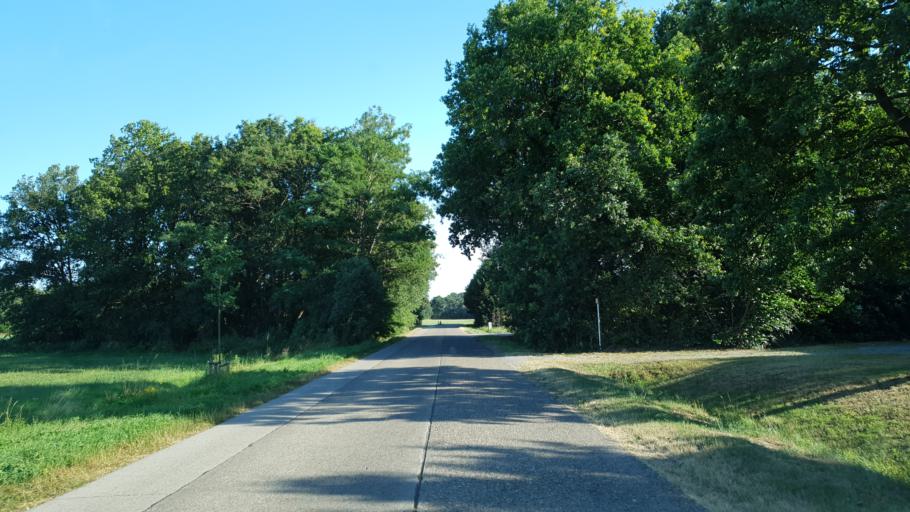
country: BE
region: Flanders
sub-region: Provincie Antwerpen
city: Merksplas
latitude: 51.3904
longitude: 4.8588
